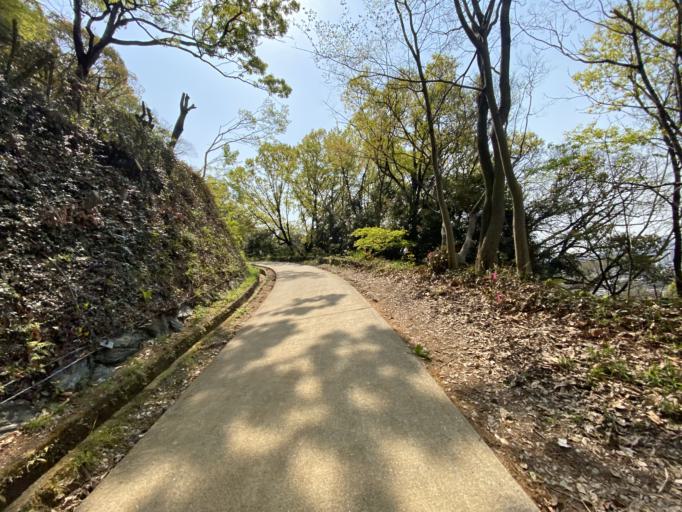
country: JP
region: Hyogo
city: Ashiya
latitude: 34.7325
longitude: 135.2756
